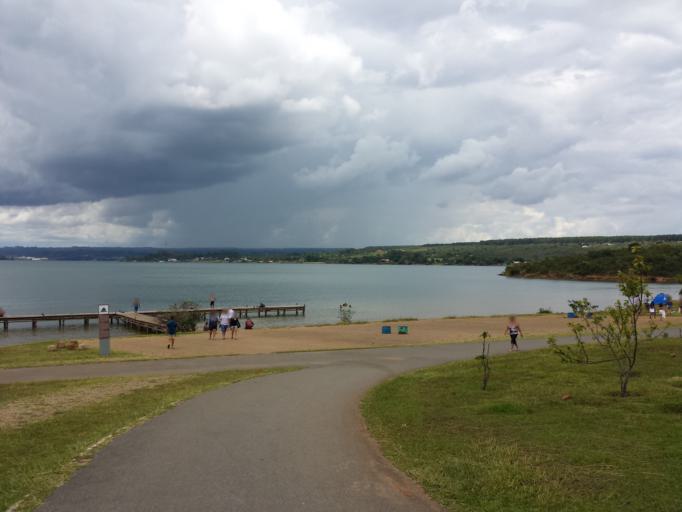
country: BR
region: Federal District
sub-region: Brasilia
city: Brasilia
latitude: -15.7973
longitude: -47.8115
